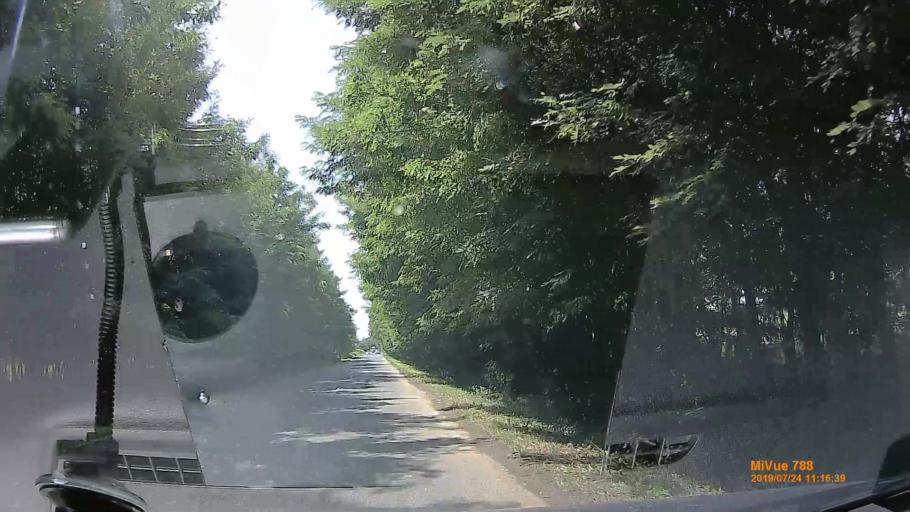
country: HU
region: Szabolcs-Szatmar-Bereg
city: Tarpa
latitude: 48.1785
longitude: 22.4637
